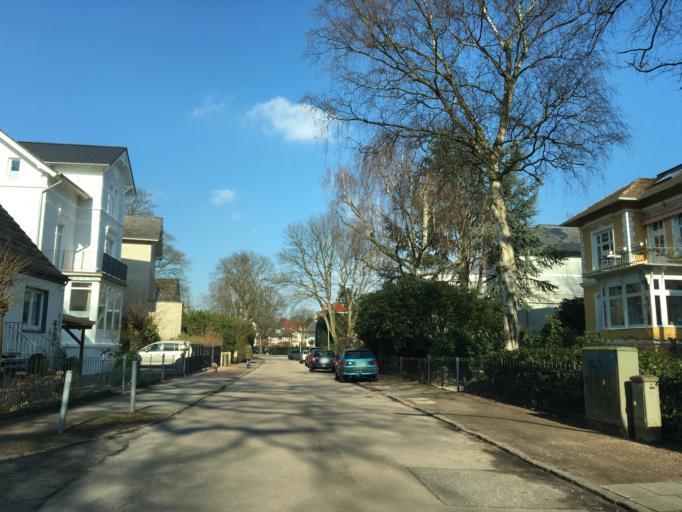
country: DE
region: Hamburg
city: Eidelstedt
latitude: 53.5608
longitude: 9.8783
